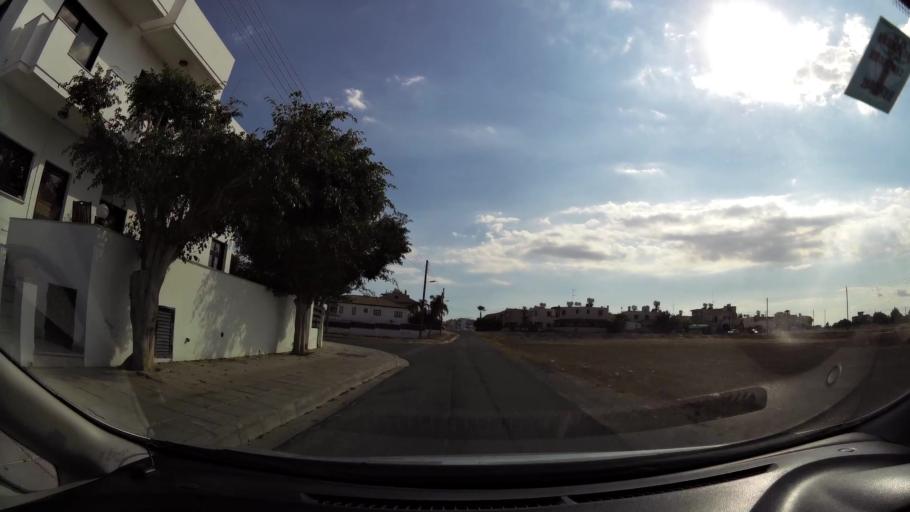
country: CY
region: Larnaka
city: Livadia
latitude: 34.9420
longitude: 33.6242
